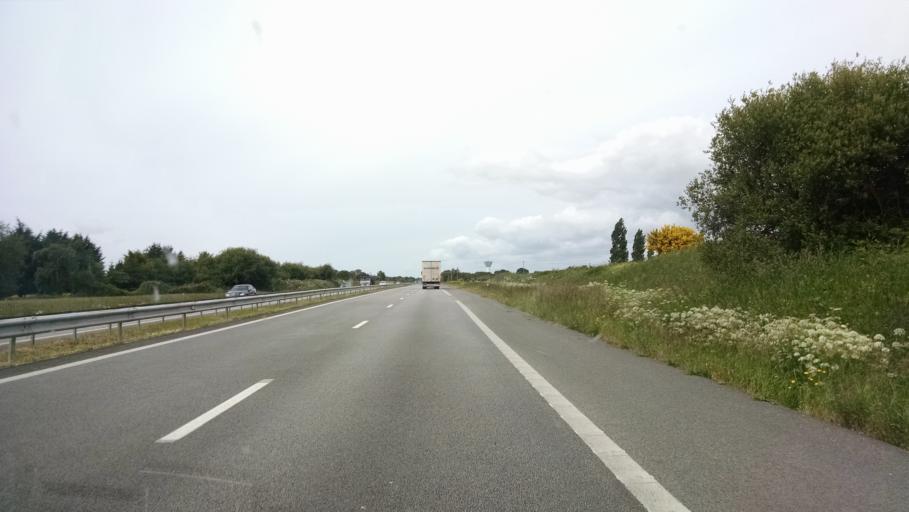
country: FR
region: Brittany
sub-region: Departement du Morbihan
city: Peaule
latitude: 47.5380
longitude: -2.3776
